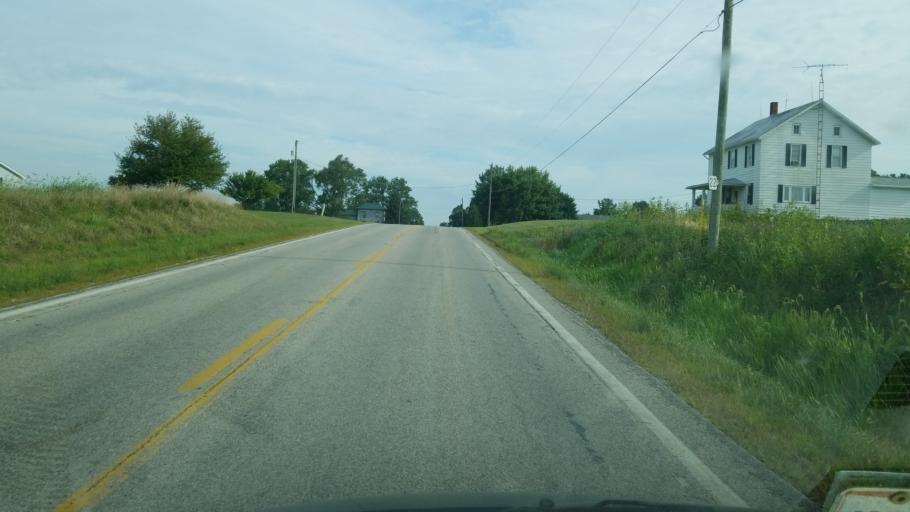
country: US
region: Ohio
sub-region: Crawford County
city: Bucyrus
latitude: 40.9020
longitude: -83.0166
